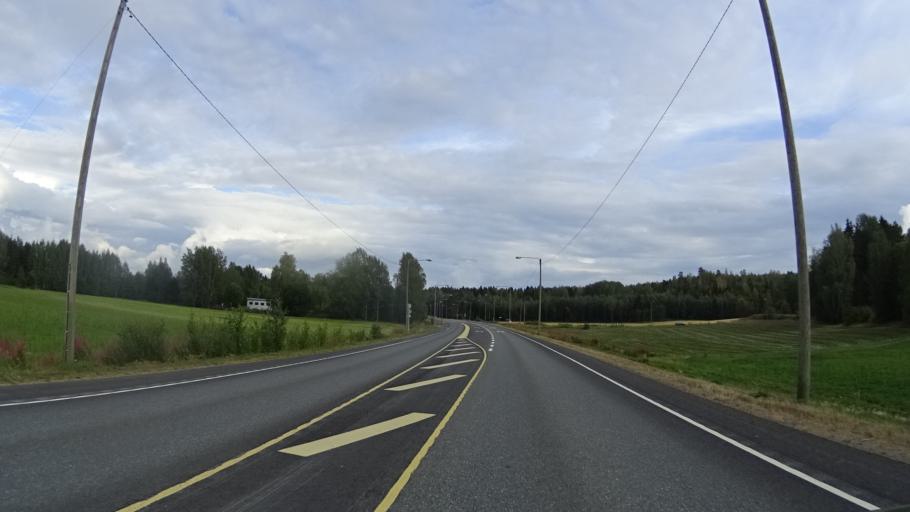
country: FI
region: Haeme
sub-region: Haemeenlinna
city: Parola
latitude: 61.0305
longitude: 24.2762
